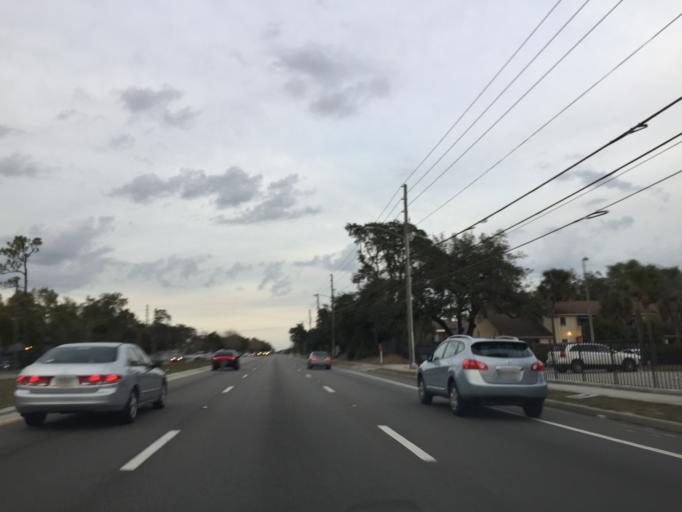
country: US
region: Florida
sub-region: Orange County
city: Alafaya
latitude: 28.5749
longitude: -81.2077
